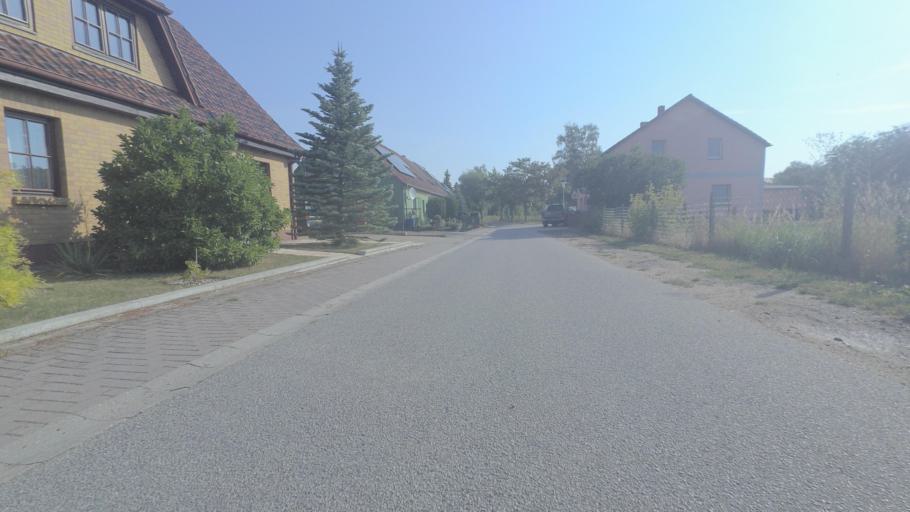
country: DE
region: Mecklenburg-Vorpommern
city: Grimmen
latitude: 54.1292
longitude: 13.0488
